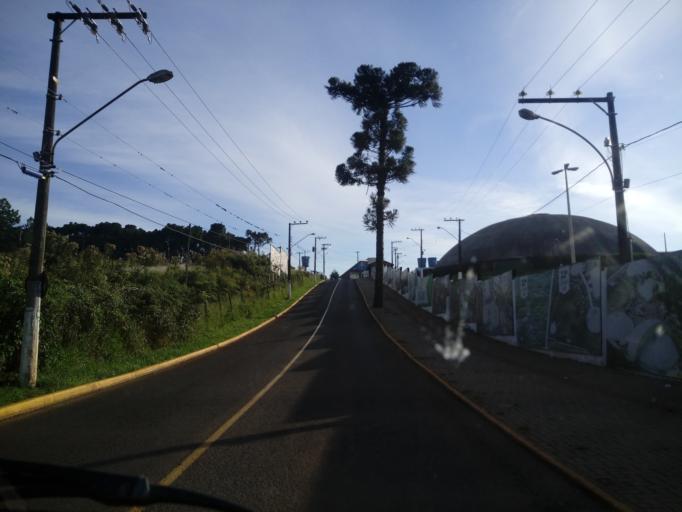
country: BR
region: Santa Catarina
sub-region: Chapeco
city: Chapeco
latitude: -27.0959
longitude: -52.6625
